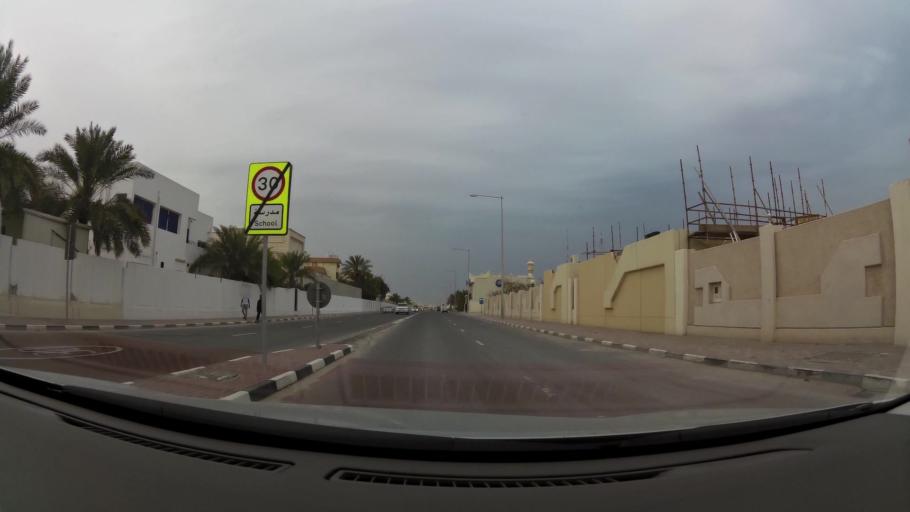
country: QA
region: Baladiyat ad Dawhah
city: Doha
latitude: 25.3300
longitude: 51.5108
